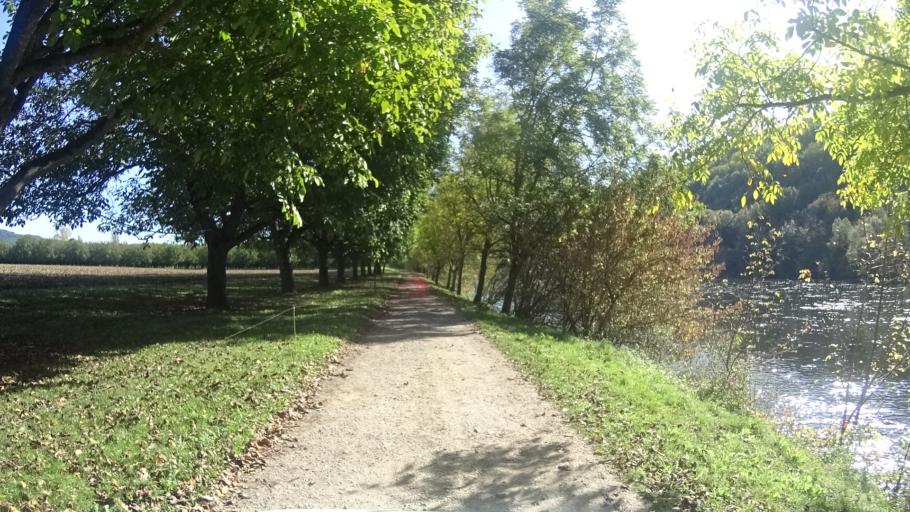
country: FR
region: Aquitaine
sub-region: Departement de la Dordogne
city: Saint-Cyprien
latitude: 44.8457
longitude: 1.0579
